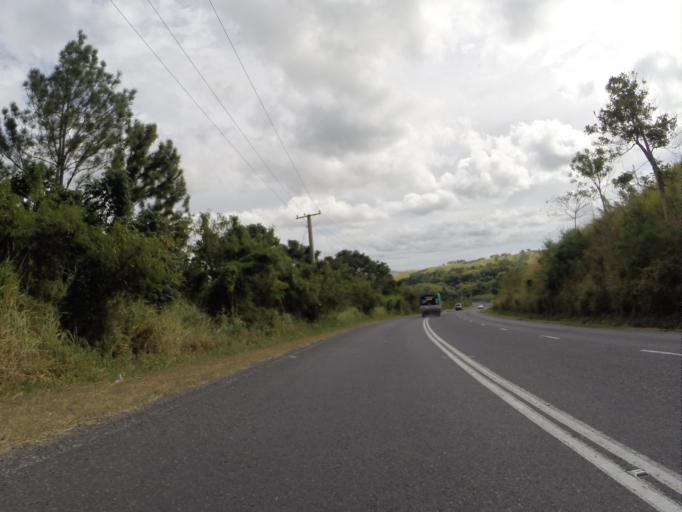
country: FJ
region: Western
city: Nadi
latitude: -18.0920
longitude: 177.3881
